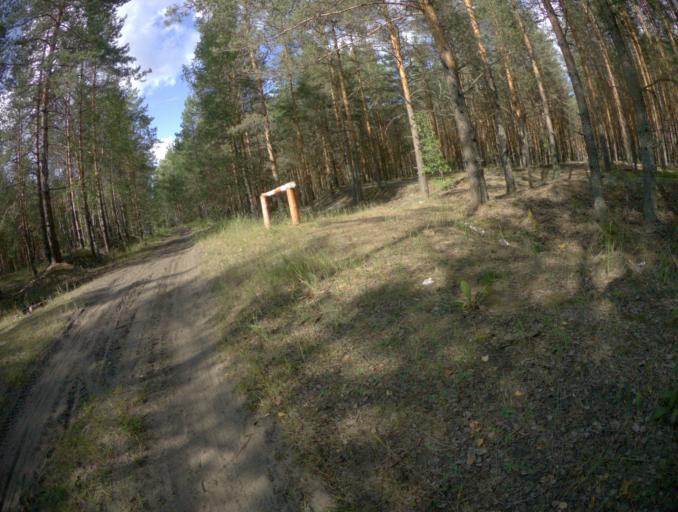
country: RU
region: Vladimir
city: Sobinka
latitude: 55.9496
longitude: 40.0590
